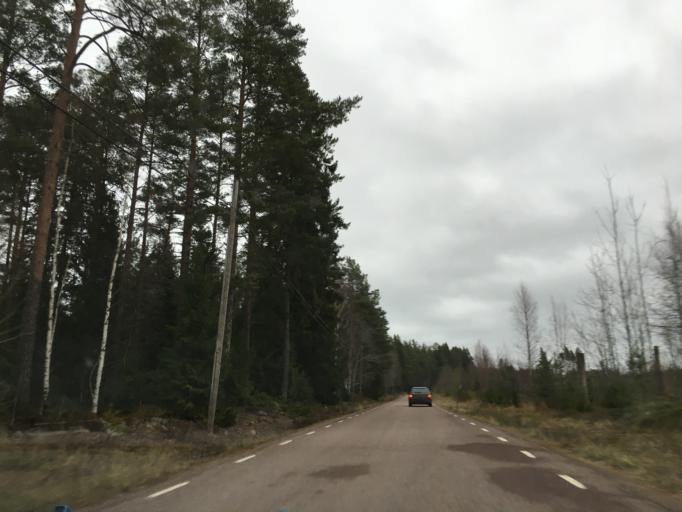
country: SE
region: Uppsala
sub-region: Alvkarleby Kommun
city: AElvkarleby
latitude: 60.6452
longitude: 17.5151
